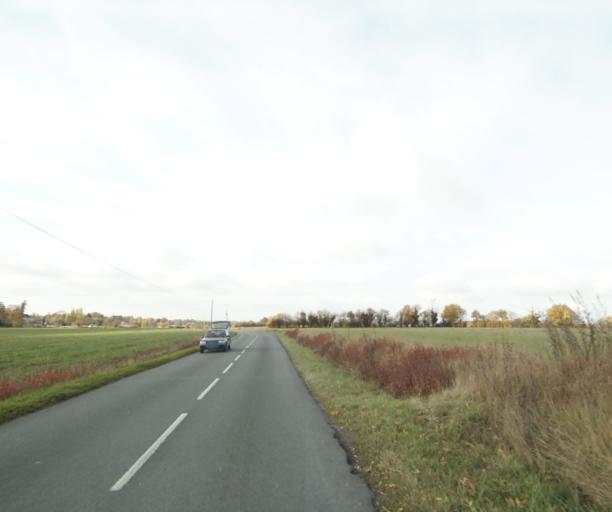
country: FR
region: Poitou-Charentes
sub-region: Departement de la Charente-Maritime
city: Saint-Georges-des-Coteaux
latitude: 45.7610
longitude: -0.6901
